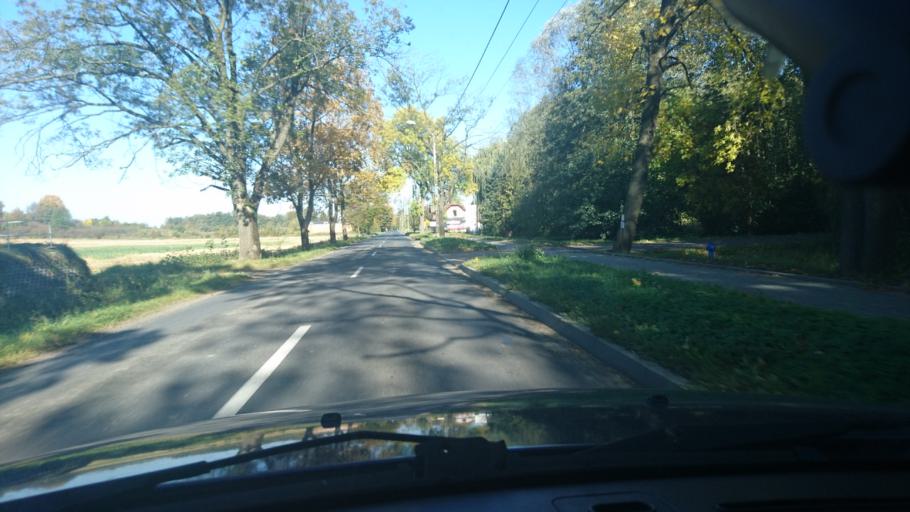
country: PL
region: Silesian Voivodeship
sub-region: Powiat bielski
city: Jasienica
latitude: 49.8235
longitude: 18.9132
